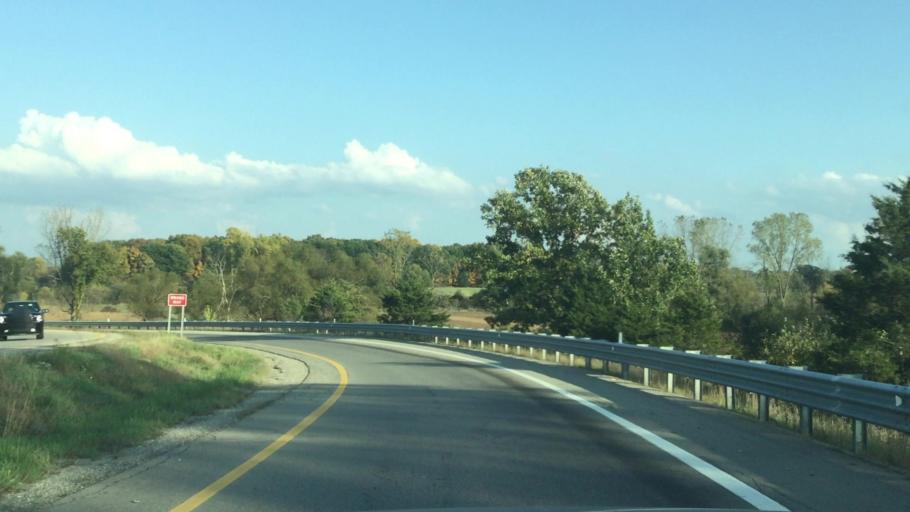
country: US
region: Michigan
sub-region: Washtenaw County
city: Chelsea
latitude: 42.2926
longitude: -84.0268
